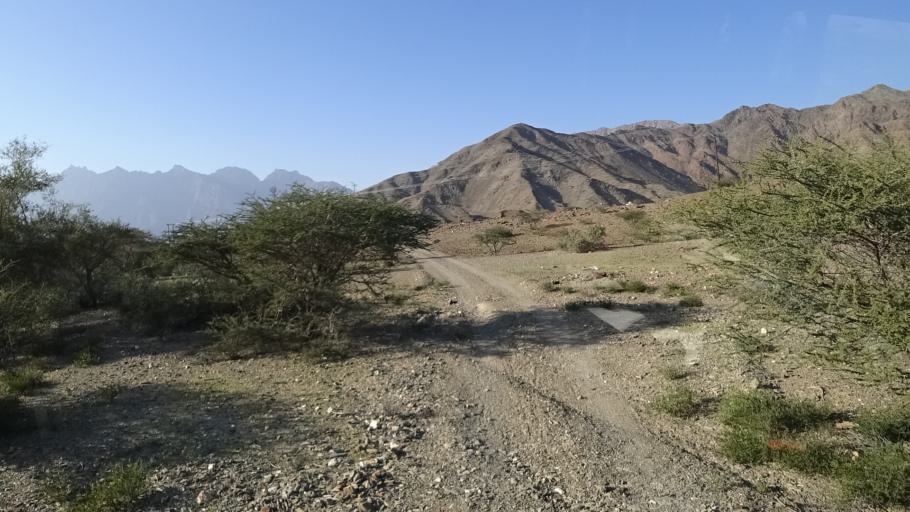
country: OM
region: Al Batinah
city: Rustaq
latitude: 23.2748
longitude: 57.3607
